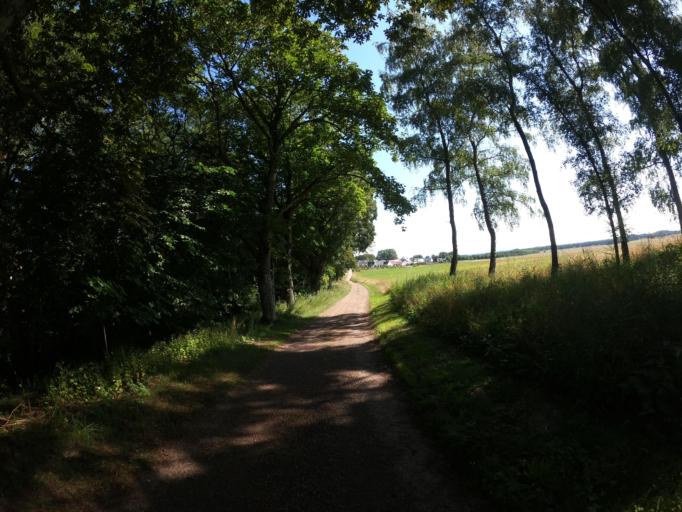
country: SE
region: Skane
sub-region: Lunds Kommun
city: Veberod
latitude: 55.6743
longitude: 13.4156
